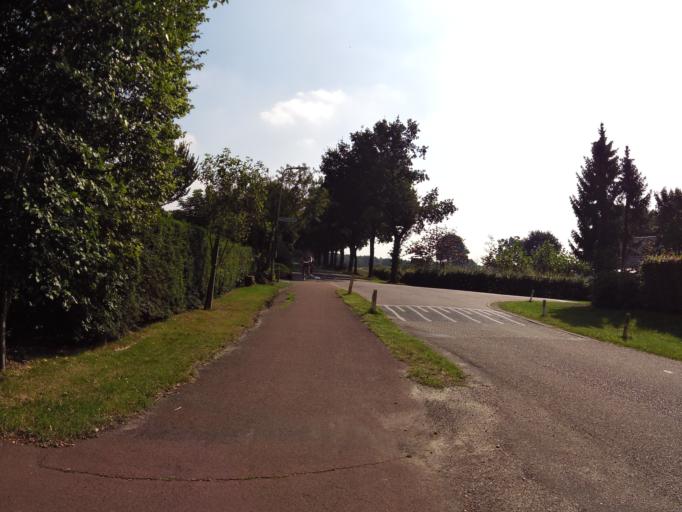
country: NL
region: Overijssel
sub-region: Gemeente Twenterand
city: Westerhaar-Vriezenveensewijk
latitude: 52.4775
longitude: 6.6446
